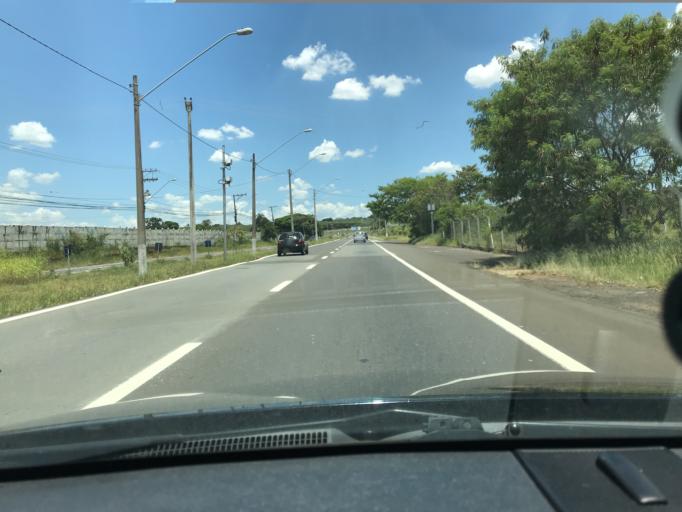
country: BR
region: Sao Paulo
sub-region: Campinas
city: Campinas
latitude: -22.8683
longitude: -47.0967
